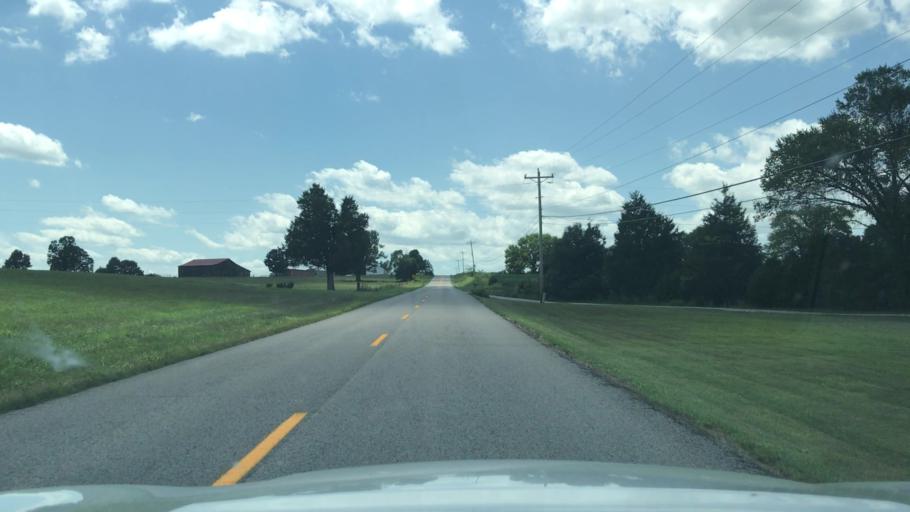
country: US
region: Kentucky
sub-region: Christian County
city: Hopkinsville
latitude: 36.9702
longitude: -87.3756
